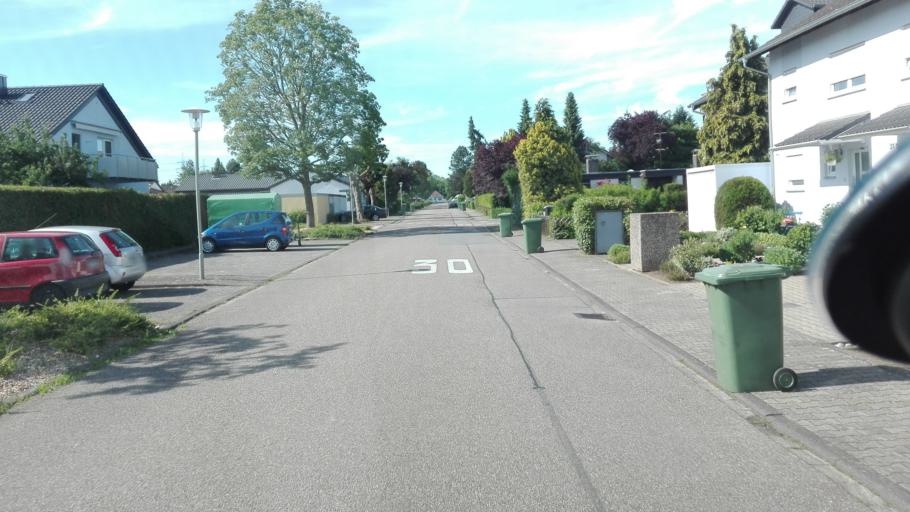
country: DE
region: Baden-Wuerttemberg
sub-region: Karlsruhe Region
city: Eggenstein-Leopoldshafen
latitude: 49.0998
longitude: 8.4067
